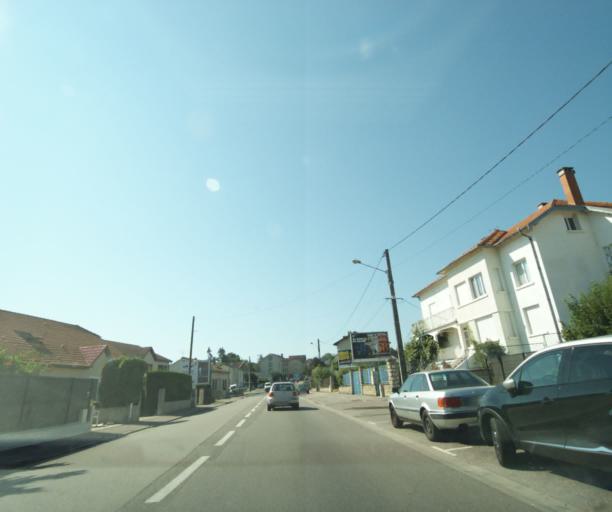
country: FR
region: Lorraine
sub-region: Departement de Meurthe-et-Moselle
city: Toul
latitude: 48.6674
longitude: 5.8819
